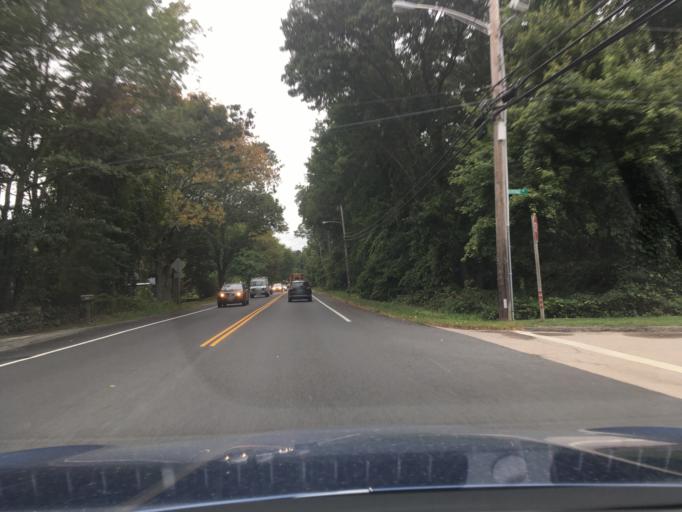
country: US
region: Rhode Island
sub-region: Kent County
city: East Greenwich
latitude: 41.6634
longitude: -71.4698
